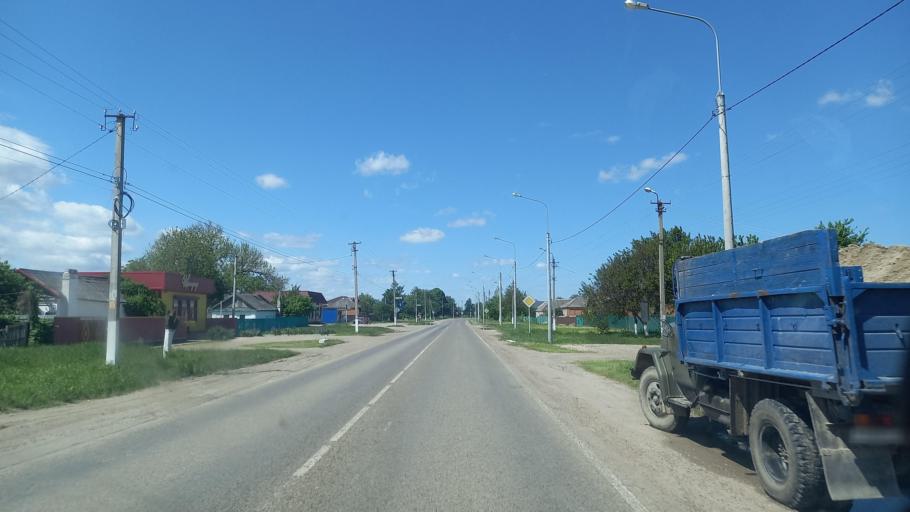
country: RU
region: Krasnodarskiy
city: Novoukrainskoye
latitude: 45.3803
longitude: 40.5404
